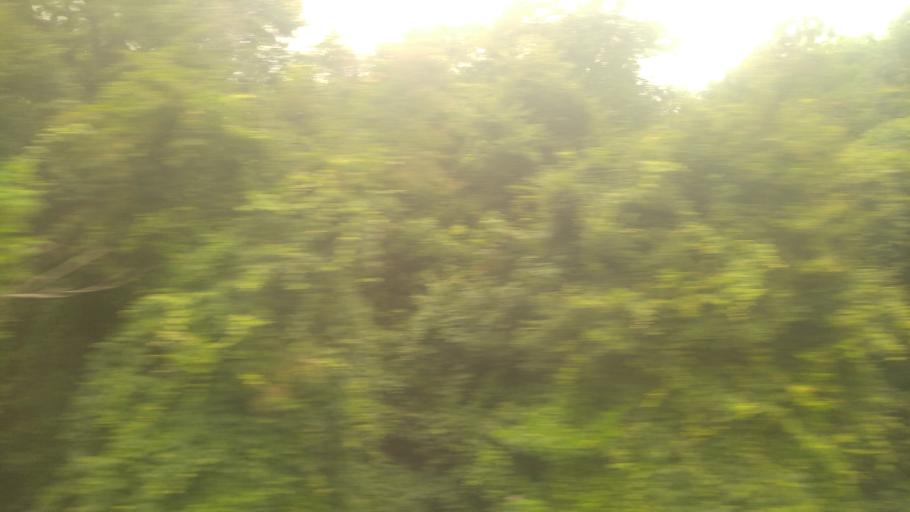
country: US
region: Virginia
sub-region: Henrico County
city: Glen Allen
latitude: 37.6668
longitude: -77.5048
